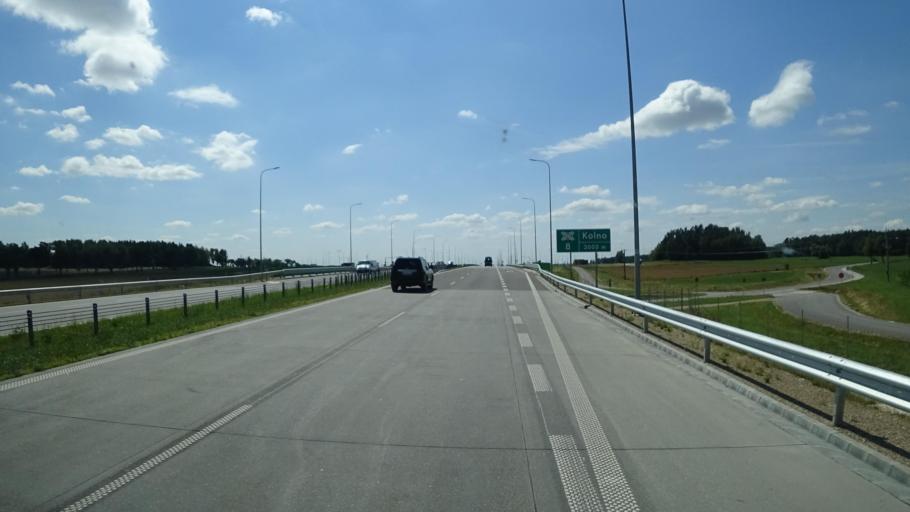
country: PL
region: Podlasie
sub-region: Powiat lomzynski
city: Piatnica
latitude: 53.2742
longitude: 22.1298
